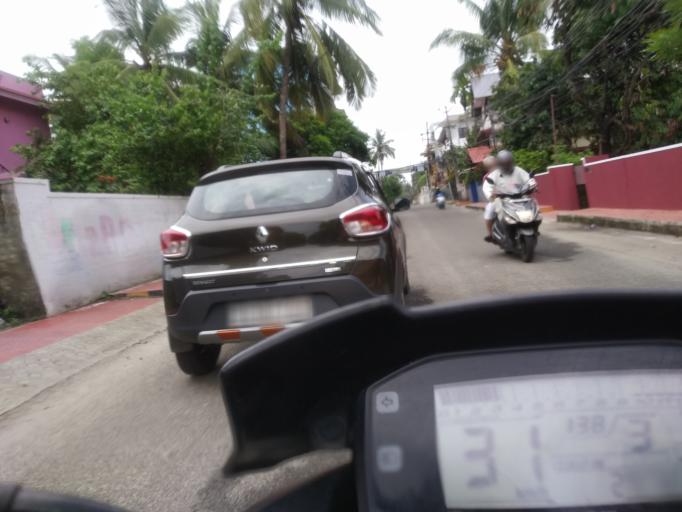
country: IN
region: Kerala
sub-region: Ernakulam
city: Elur
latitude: 10.0125
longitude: 76.2928
